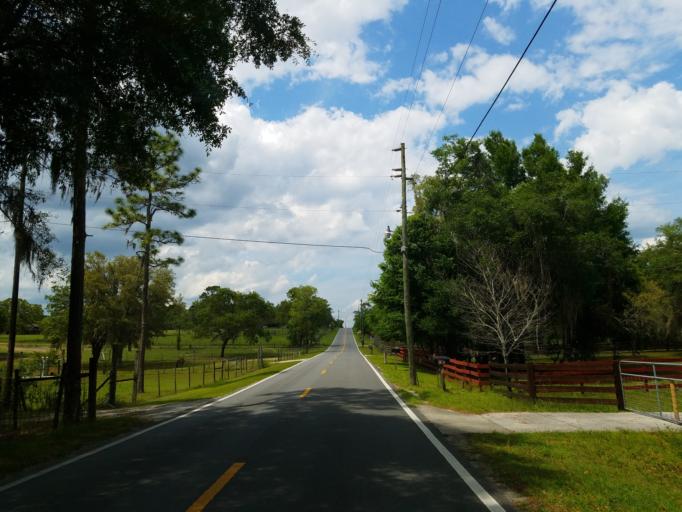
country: US
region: Florida
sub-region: Hernando County
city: Hill 'n Dale
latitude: 28.5326
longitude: -82.2759
